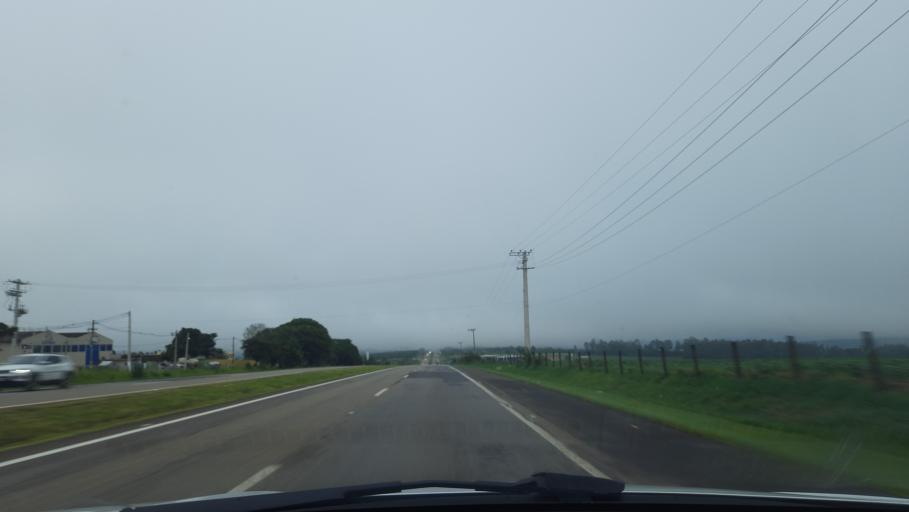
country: BR
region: Sao Paulo
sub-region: Casa Branca
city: Casa Branca
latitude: -21.7573
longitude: -47.0707
